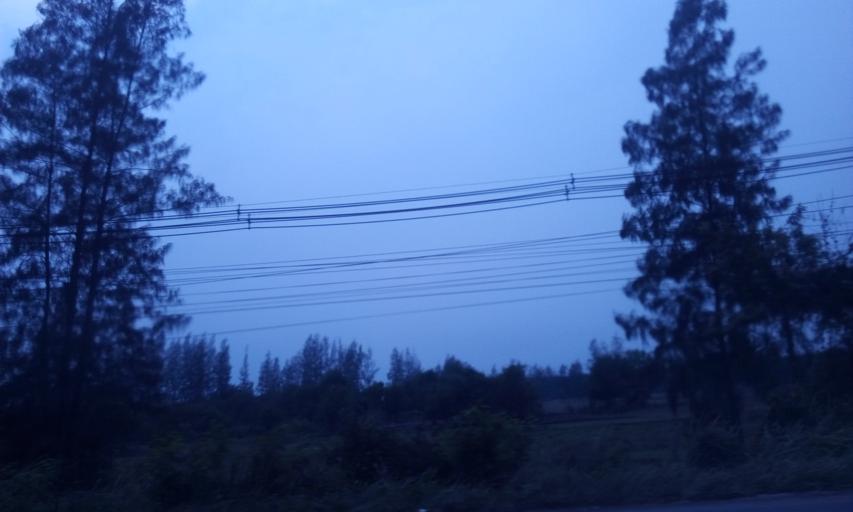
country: TH
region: Chon Buri
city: Ko Chan
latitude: 13.3037
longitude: 101.2630
